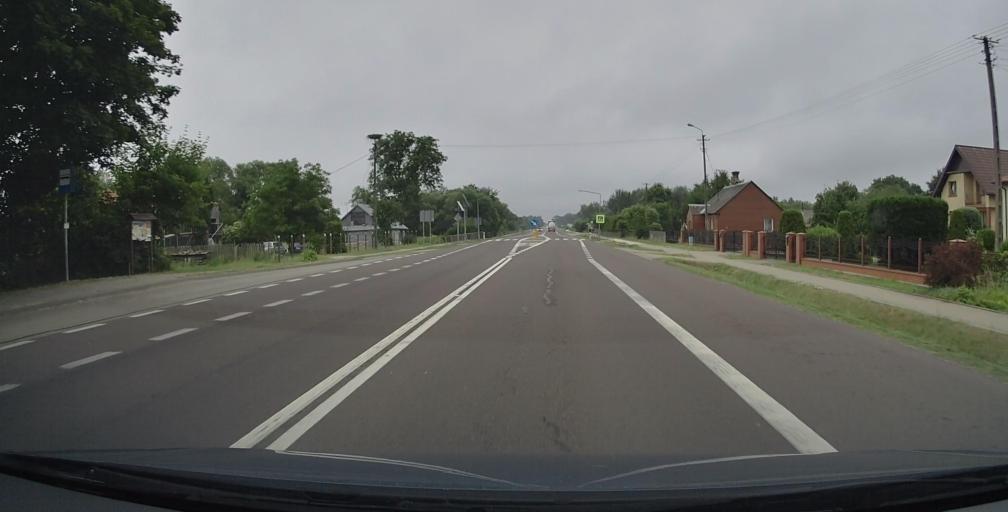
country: PL
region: Lublin Voivodeship
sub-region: Powiat bialski
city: Zalesie
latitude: 52.0369
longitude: 23.4538
